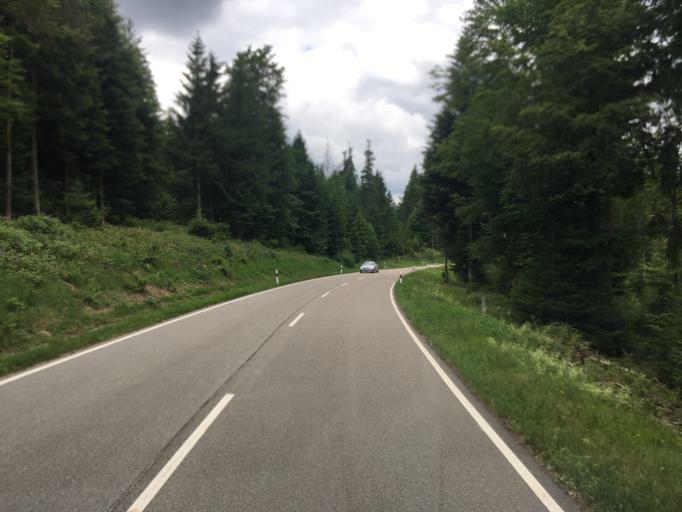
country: DE
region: Baden-Wuerttemberg
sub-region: Karlsruhe Region
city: Biberach
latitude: 48.6562
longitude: 8.2984
